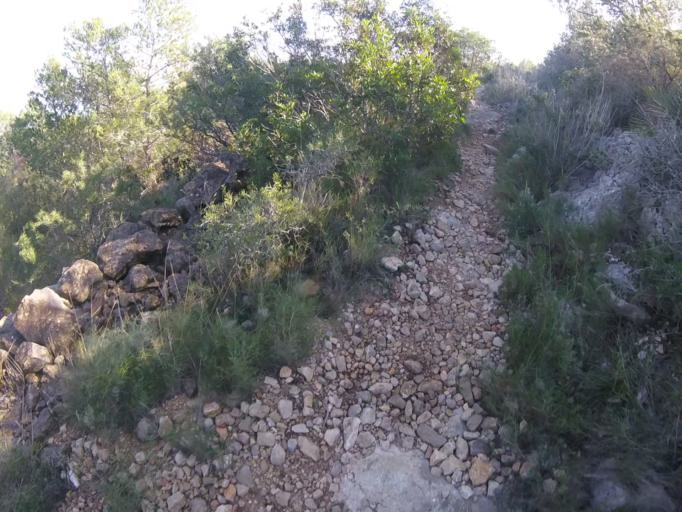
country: ES
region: Valencia
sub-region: Provincia de Castello
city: Santa Magdalena de Pulpis
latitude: 40.2994
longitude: 0.3316
